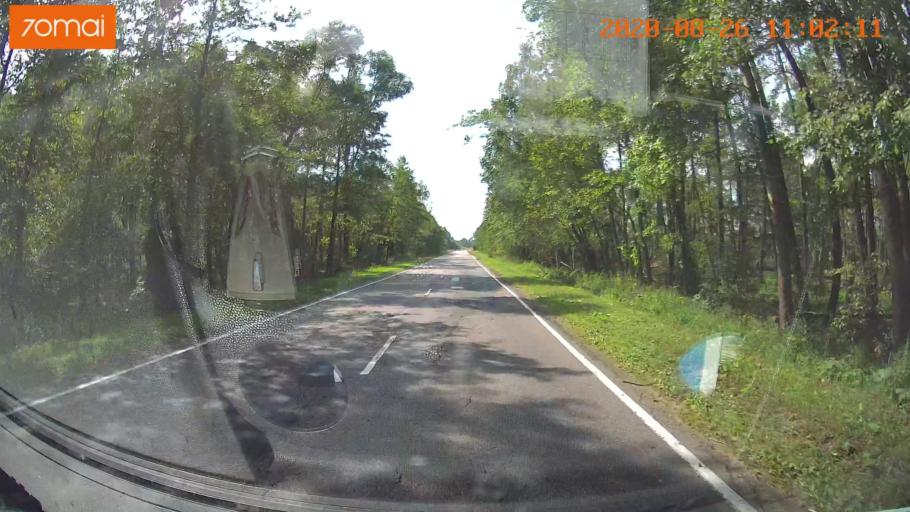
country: RU
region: Rjazan
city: Izhevskoye
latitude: 54.5539
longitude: 41.2256
